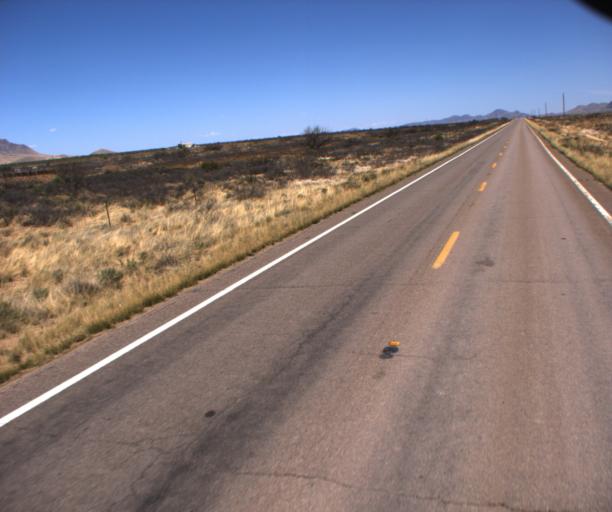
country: US
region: Arizona
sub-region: Cochise County
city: Douglas
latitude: 31.7496
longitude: -109.0918
